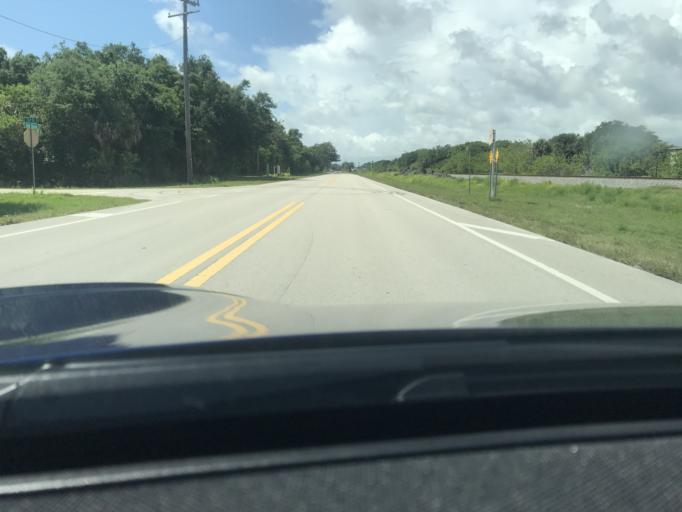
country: US
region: Florida
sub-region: Indian River County
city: Winter Beach
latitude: 27.7229
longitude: -80.4239
